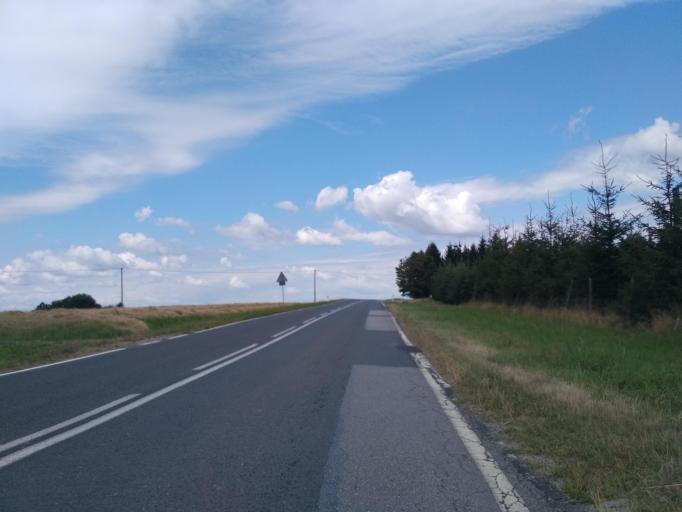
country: PL
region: Subcarpathian Voivodeship
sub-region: Powiat przeworski
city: Jawornik Polski
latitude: 49.8916
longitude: 22.2351
